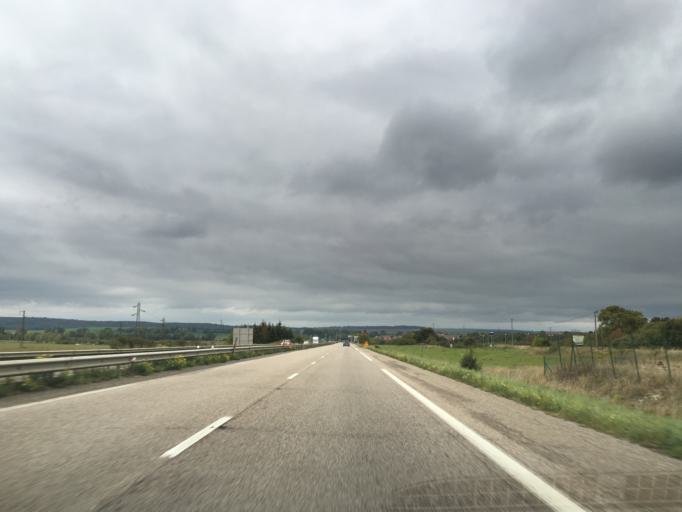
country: FR
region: Lorraine
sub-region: Departement de Meurthe-et-Moselle
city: Foug
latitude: 48.6826
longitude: 5.7384
